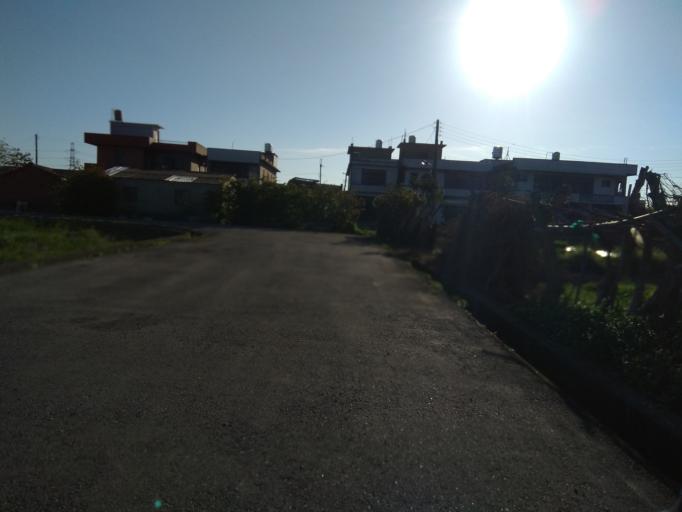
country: TW
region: Taiwan
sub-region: Hsinchu
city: Zhubei
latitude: 24.9945
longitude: 121.0524
